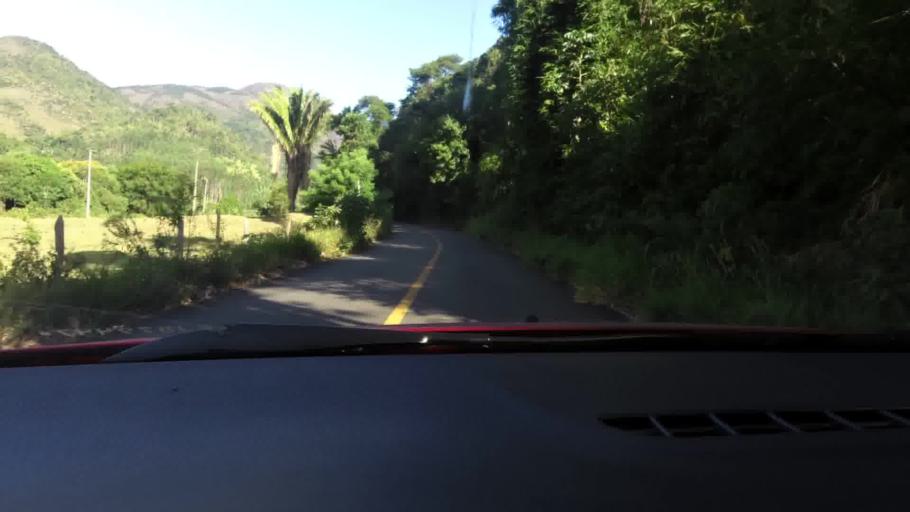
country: BR
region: Espirito Santo
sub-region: Guarapari
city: Guarapari
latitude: -20.5757
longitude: -40.5425
